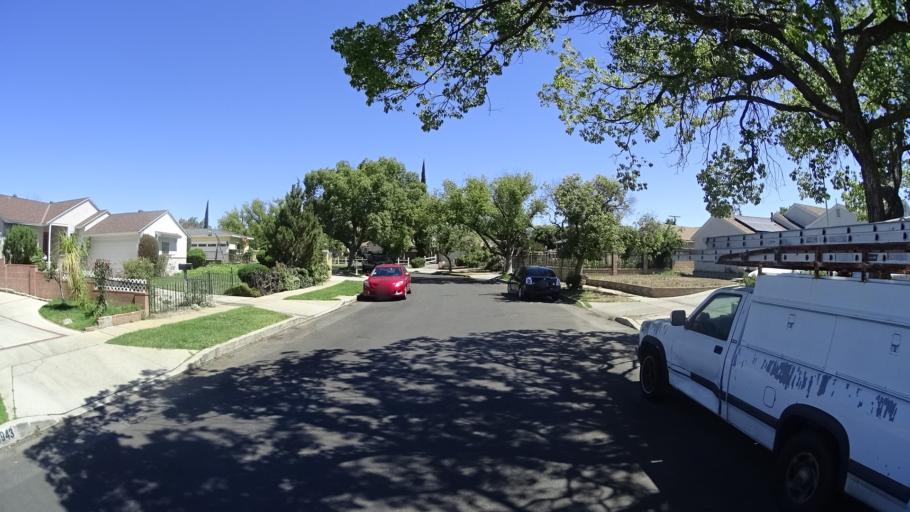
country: US
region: California
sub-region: Los Angeles County
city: San Fernando
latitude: 34.2514
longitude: -118.4533
